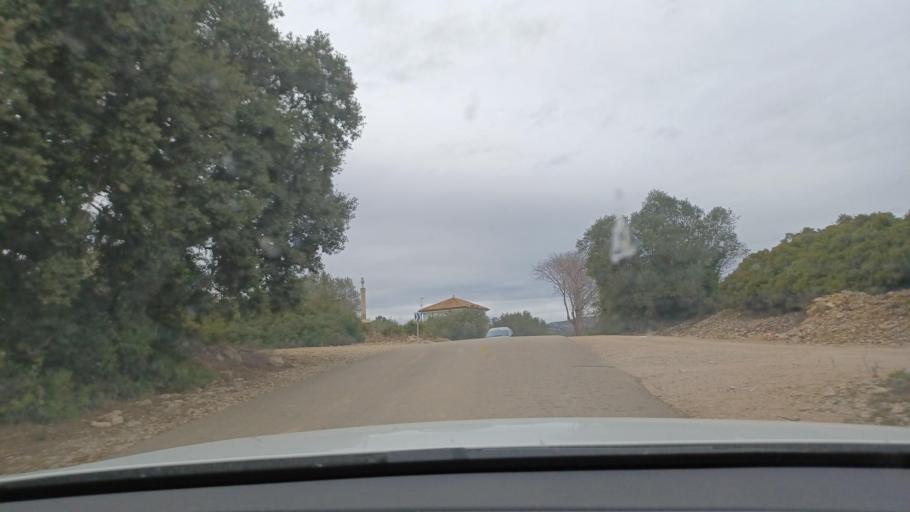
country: ES
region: Valencia
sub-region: Provincia de Castello
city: Traiguera
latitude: 40.5052
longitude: 0.2954
